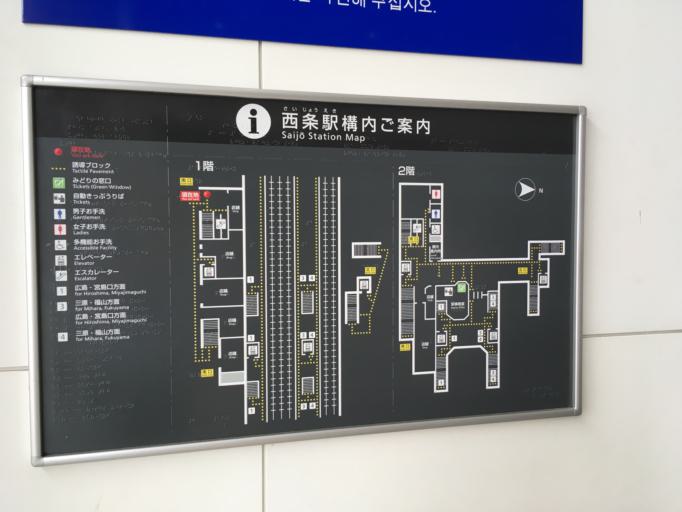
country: JP
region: Hiroshima
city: Takehara
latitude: 34.4307
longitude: 132.7432
